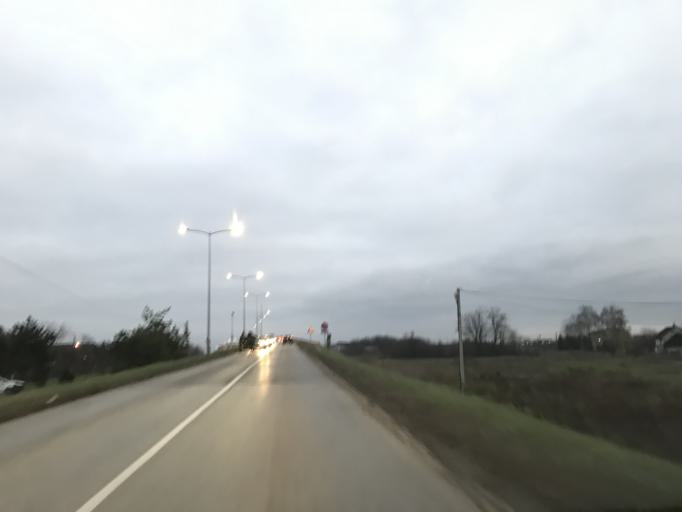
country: RS
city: Veternik
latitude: 45.2819
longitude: 19.7763
